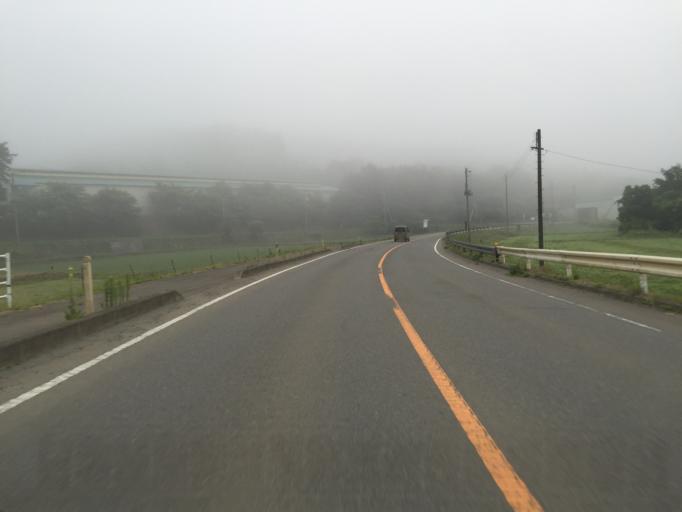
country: JP
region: Miyagi
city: Marumori
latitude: 37.7755
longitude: 140.7491
